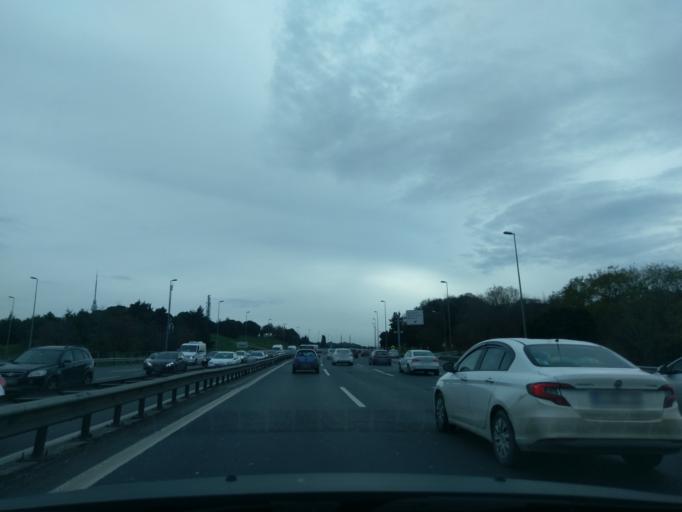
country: TR
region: Istanbul
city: UEskuedar
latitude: 41.0347
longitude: 29.0445
